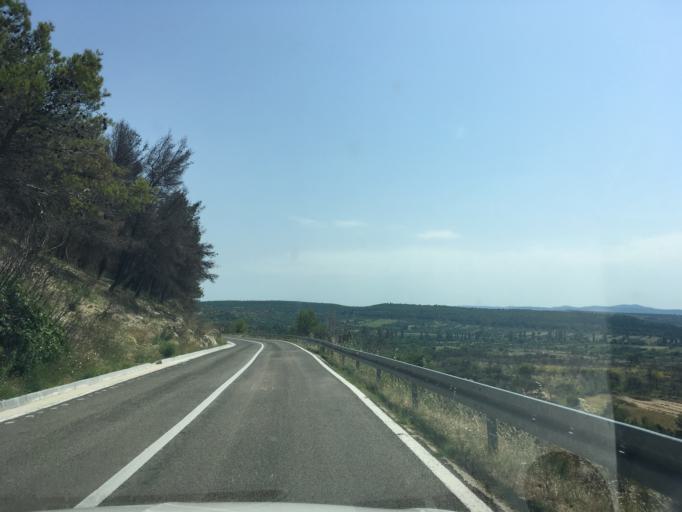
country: HR
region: Sibensko-Kniniska
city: Kistanje
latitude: 43.9412
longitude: 15.8320
